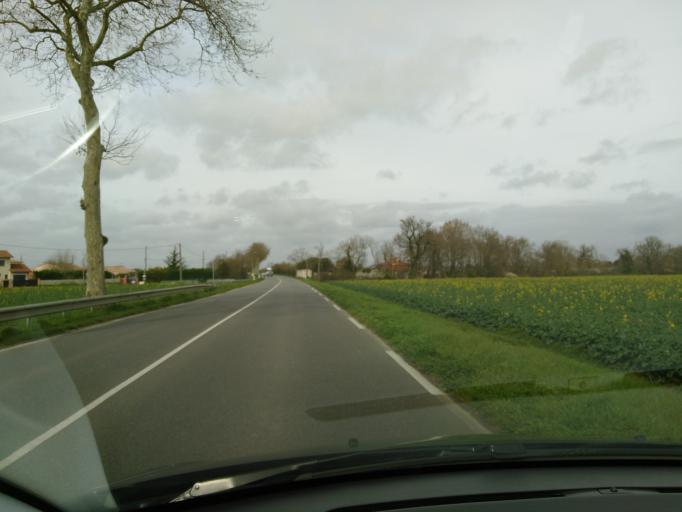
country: FR
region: Midi-Pyrenees
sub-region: Departement de la Haute-Garonne
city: Seilh
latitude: 43.7056
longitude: 1.3435
